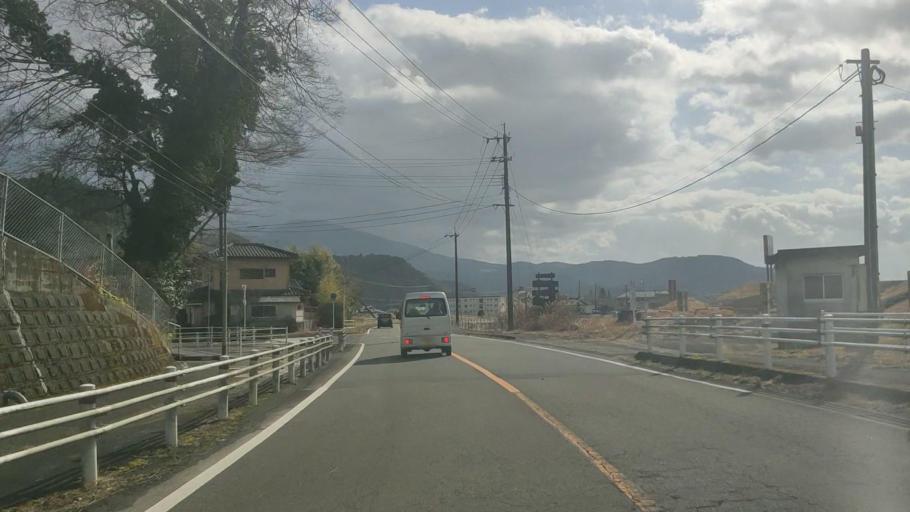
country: JP
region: Kagoshima
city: Okuchi-shinohara
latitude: 32.0214
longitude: 130.7432
